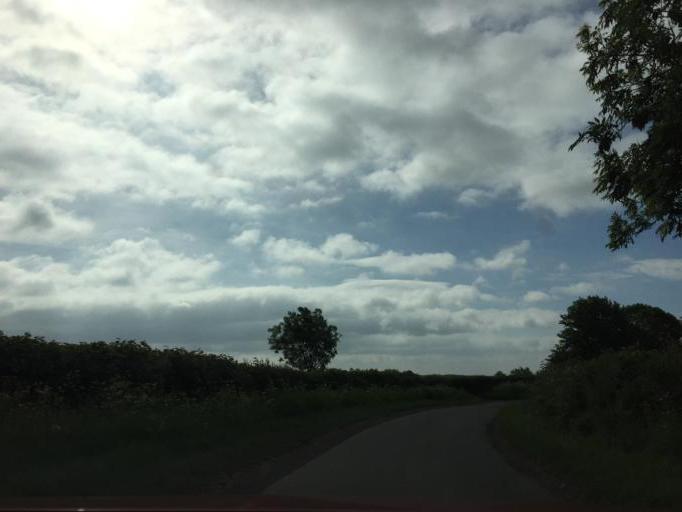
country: GB
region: England
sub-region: Northamptonshire
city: Blisworth
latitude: 52.1471
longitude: -0.9433
